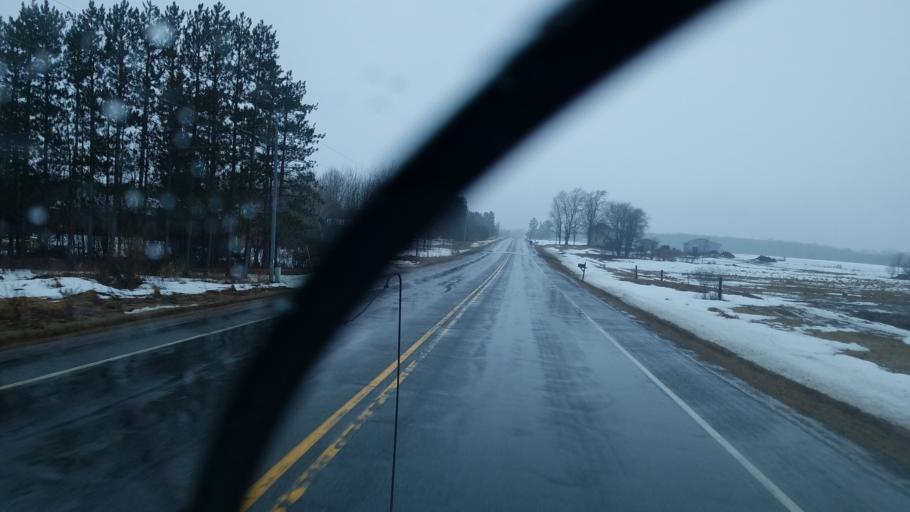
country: US
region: Wisconsin
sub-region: Marathon County
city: Spencer
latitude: 44.6778
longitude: -90.2665
